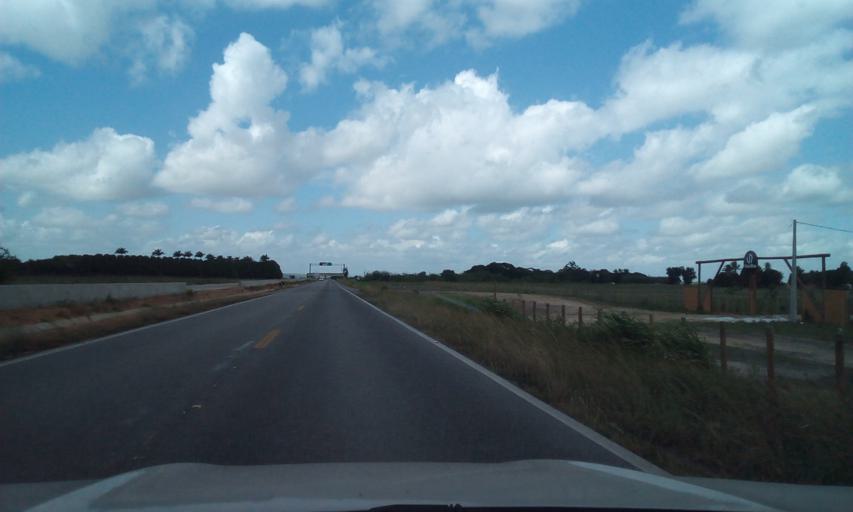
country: BR
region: Alagoas
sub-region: Pilar
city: Pilar
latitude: -9.5733
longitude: -35.9714
